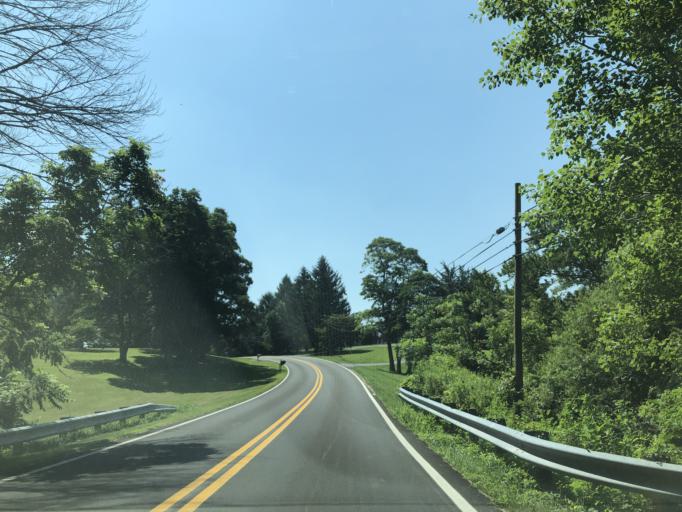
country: US
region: Maryland
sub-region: Carroll County
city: Eldersburg
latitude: 39.4546
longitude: -76.9767
